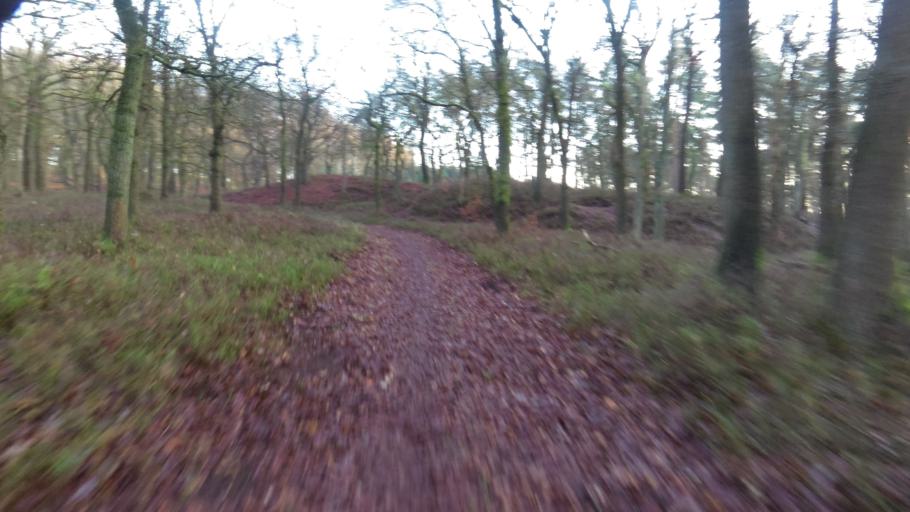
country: NL
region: Gelderland
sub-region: Gemeente Apeldoorn
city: Uddel
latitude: 52.2274
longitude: 5.8112
